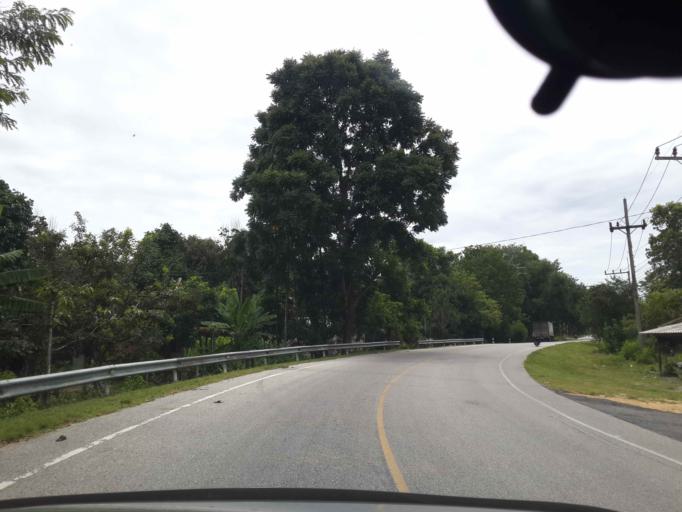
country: TH
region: Narathiwat
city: Rueso
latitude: 6.3640
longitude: 101.6075
